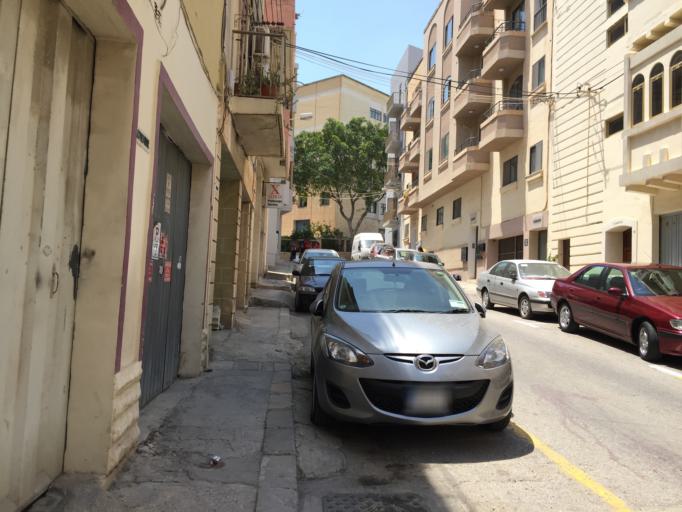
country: MT
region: Tal-Pieta
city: Pieta
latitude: 35.8936
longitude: 14.4899
